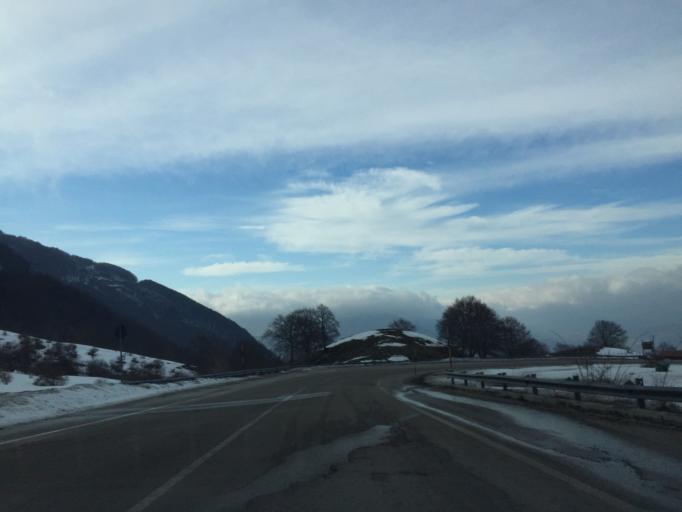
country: IT
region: Molise
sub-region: Provincia di Campobasso
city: San Massimo
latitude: 41.4656
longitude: 14.4154
